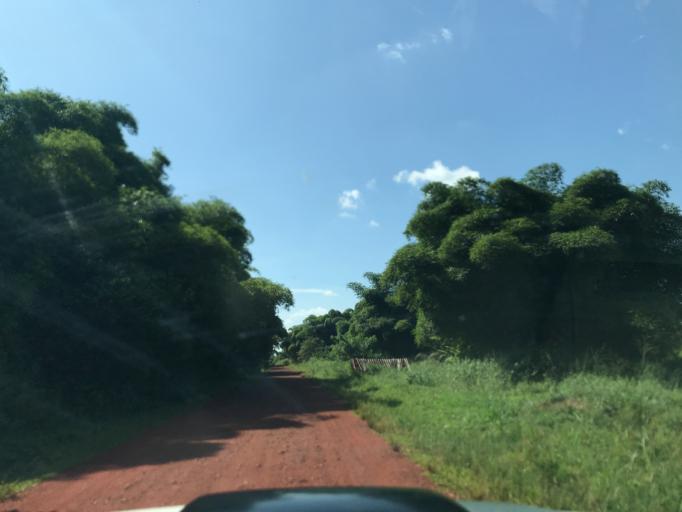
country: CD
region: Eastern Province
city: Kisangani
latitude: 1.2771
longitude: 25.2778
